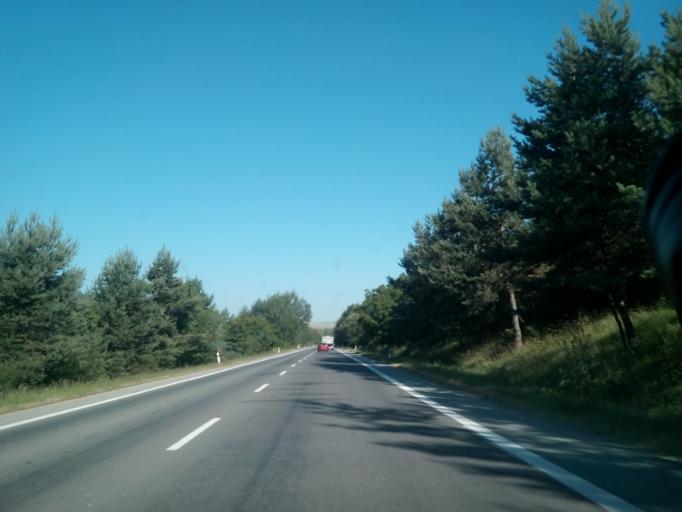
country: SK
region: Presovsky
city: Sabinov
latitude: 49.0134
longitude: 21.0481
